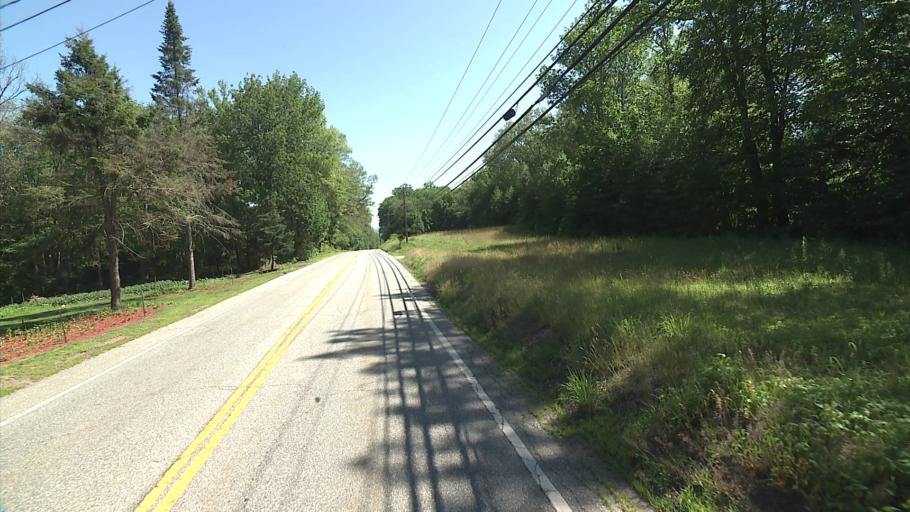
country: US
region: Connecticut
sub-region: Windham County
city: Willimantic
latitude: 41.6896
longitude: -72.2278
